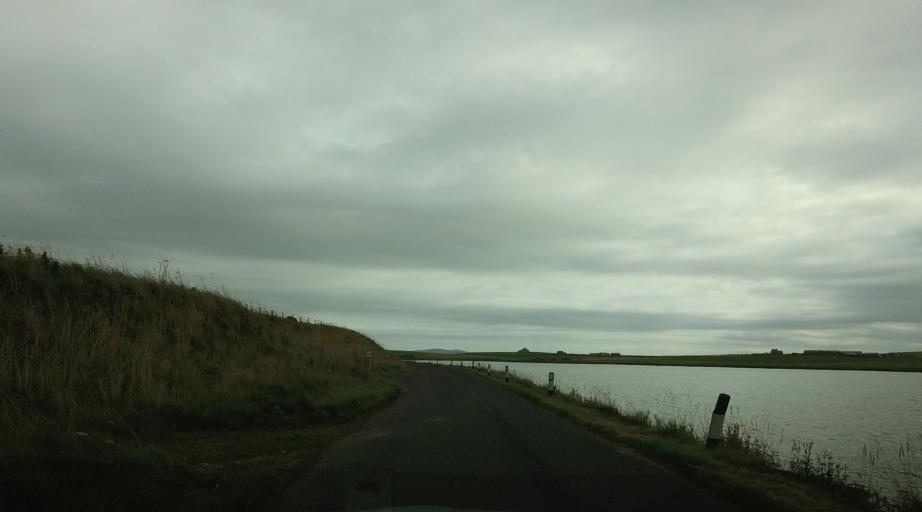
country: GB
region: Scotland
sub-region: Orkney Islands
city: Stromness
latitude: 59.0445
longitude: -3.3176
